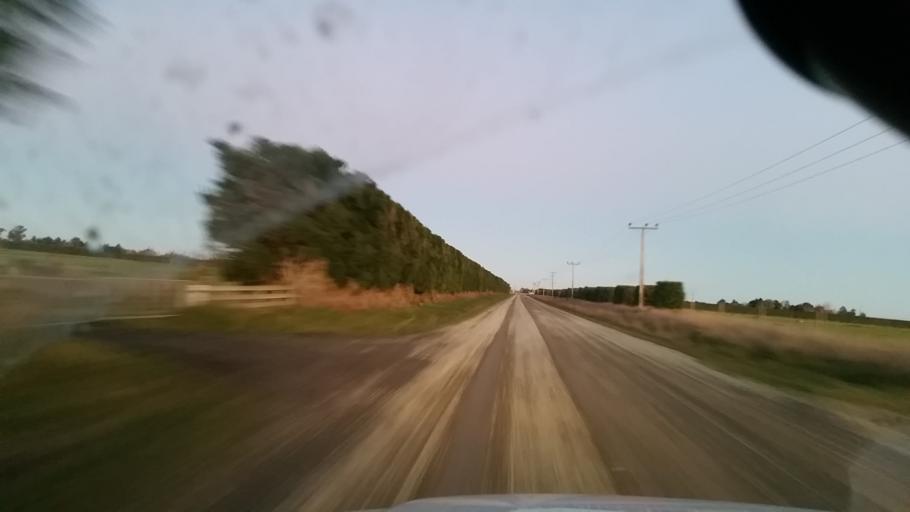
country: NZ
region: Canterbury
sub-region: Ashburton District
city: Tinwald
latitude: -43.9871
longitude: 171.6540
